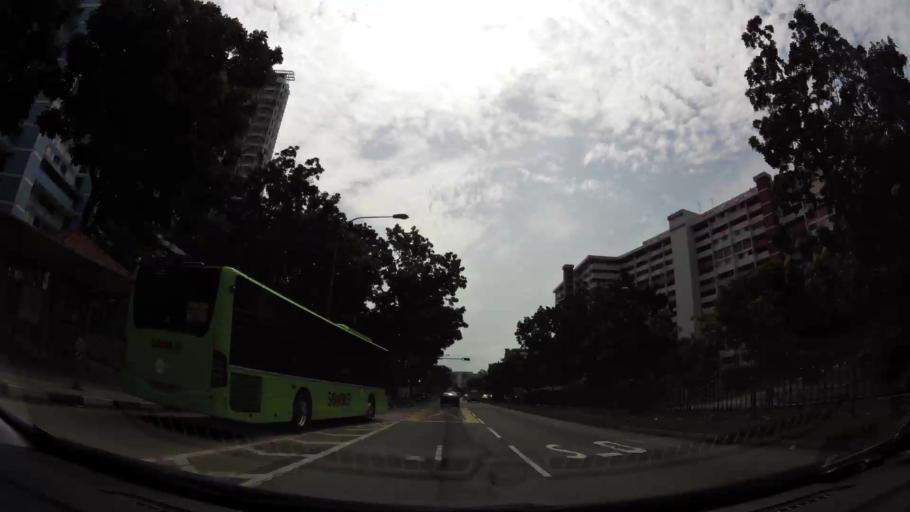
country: SG
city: Singapore
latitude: 1.3097
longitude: 103.7599
